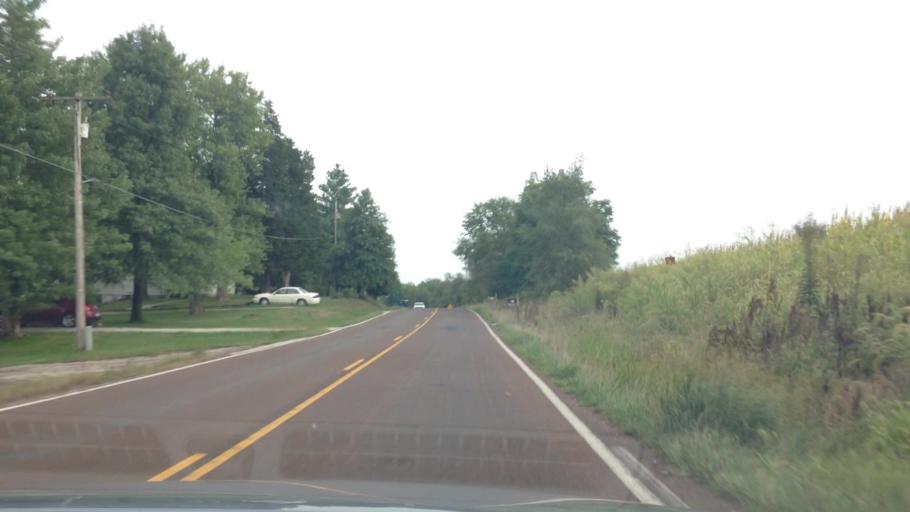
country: US
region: Missouri
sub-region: Clay County
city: Smithville
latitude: 39.4011
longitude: -94.5892
